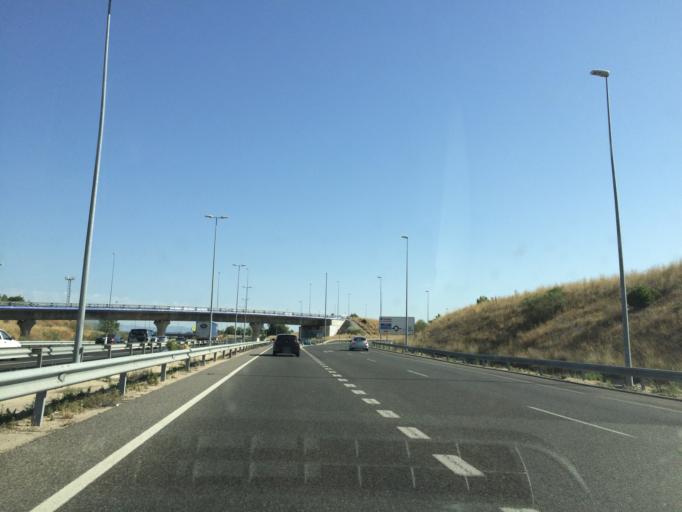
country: ES
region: Madrid
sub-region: Provincia de Madrid
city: Majadahonda
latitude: 40.4495
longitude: -3.8792
